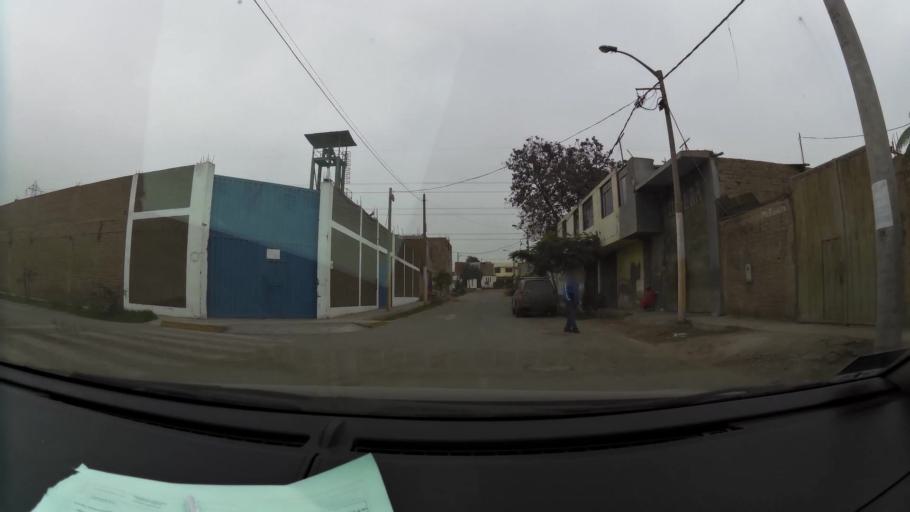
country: PE
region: Lima
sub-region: Lima
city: Urb. Santo Domingo
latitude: -11.8769
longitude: -77.0672
